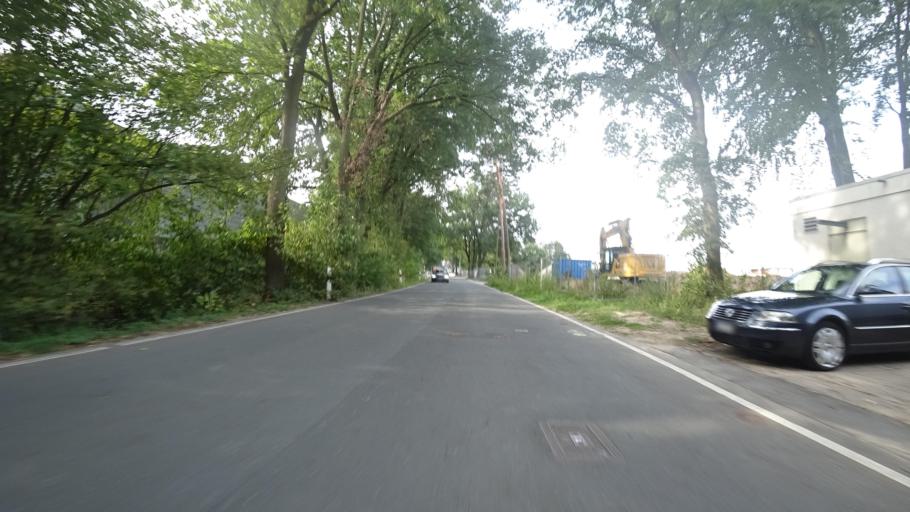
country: DE
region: North Rhine-Westphalia
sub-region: Regierungsbezirk Detmold
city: Steinhagen
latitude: 51.9621
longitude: 8.4559
